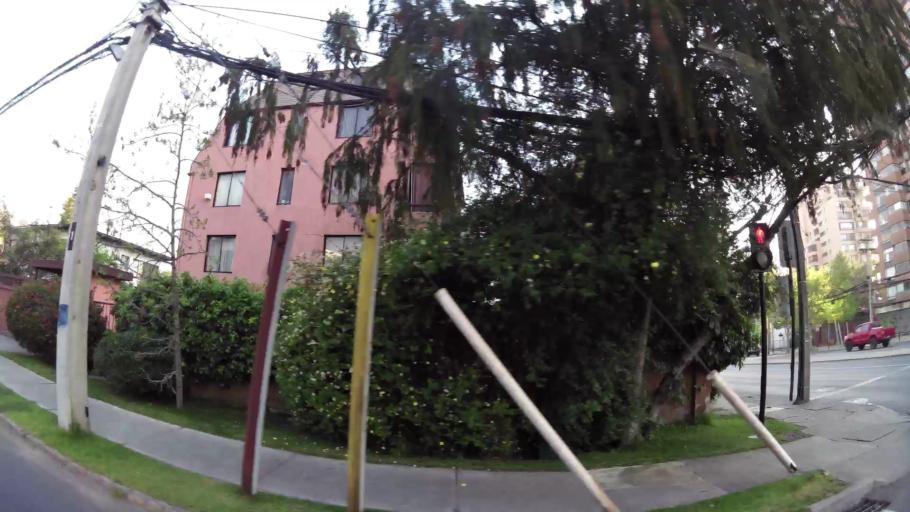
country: CL
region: Santiago Metropolitan
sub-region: Provincia de Santiago
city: Villa Presidente Frei, Nunoa, Santiago, Chile
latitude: -33.3904
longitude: -70.5411
